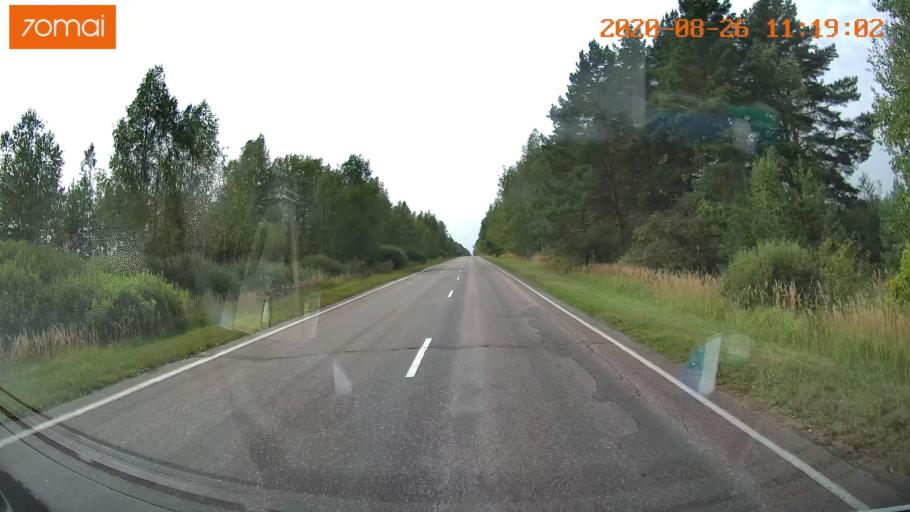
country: RU
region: Rjazan
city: Shilovo
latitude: 54.4038
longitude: 41.0868
